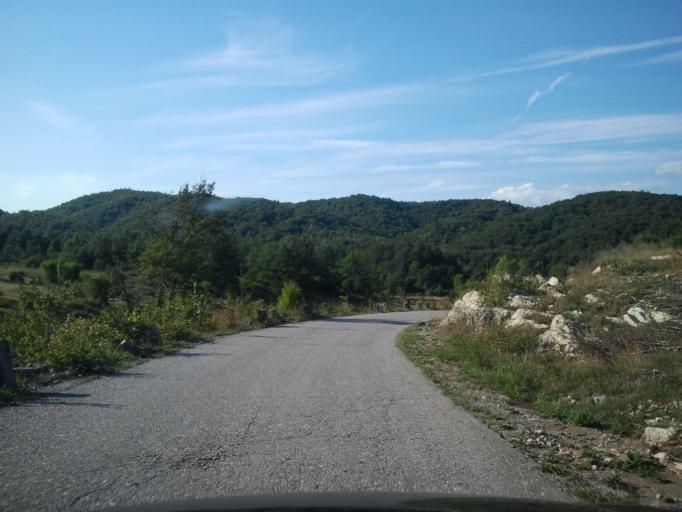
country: HR
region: Zadarska
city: Obrovac
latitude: 44.3307
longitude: 15.6397
